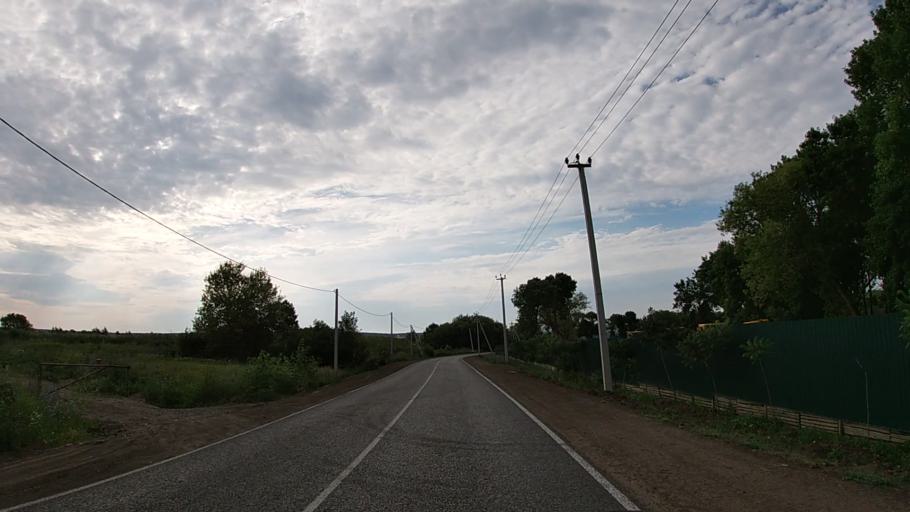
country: RU
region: Belgorod
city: Severnyy
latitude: 50.7191
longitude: 36.5870
